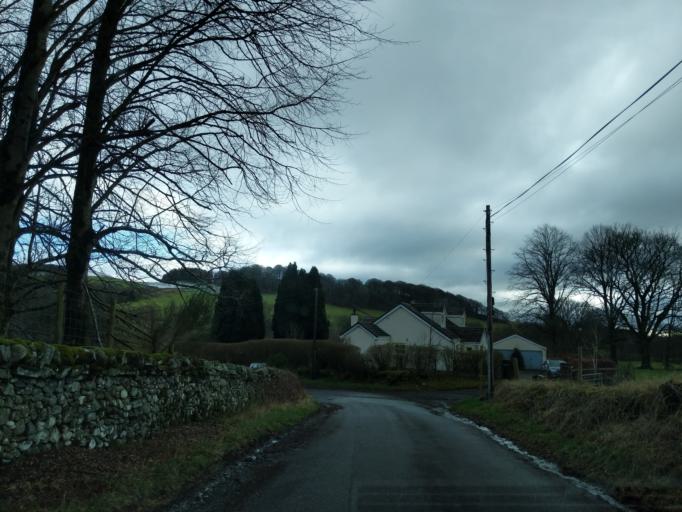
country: GB
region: Scotland
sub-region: Dumfries and Galloway
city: Moffat
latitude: 55.3171
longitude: -3.4225
